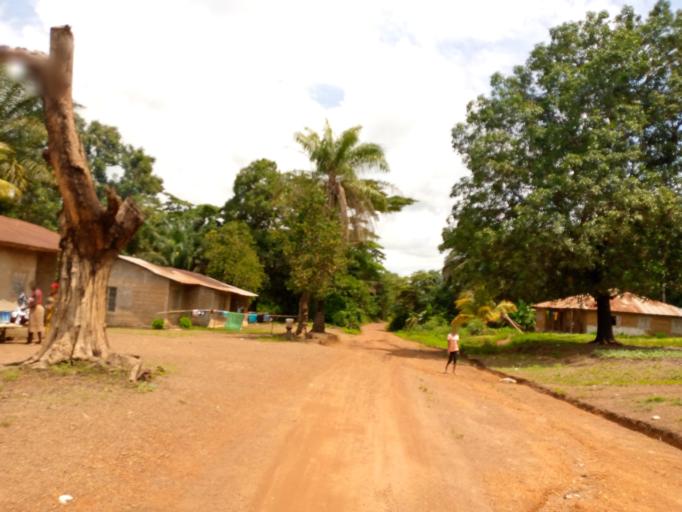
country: SL
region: Northern Province
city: Magburaka
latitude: 8.7064
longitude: -11.9652
